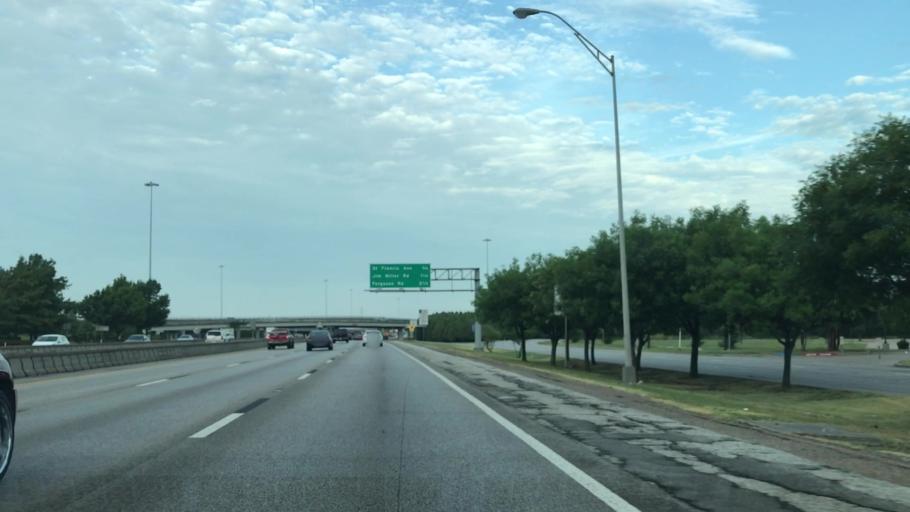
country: US
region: Texas
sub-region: Dallas County
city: Mesquite
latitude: 32.8017
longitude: -96.6729
